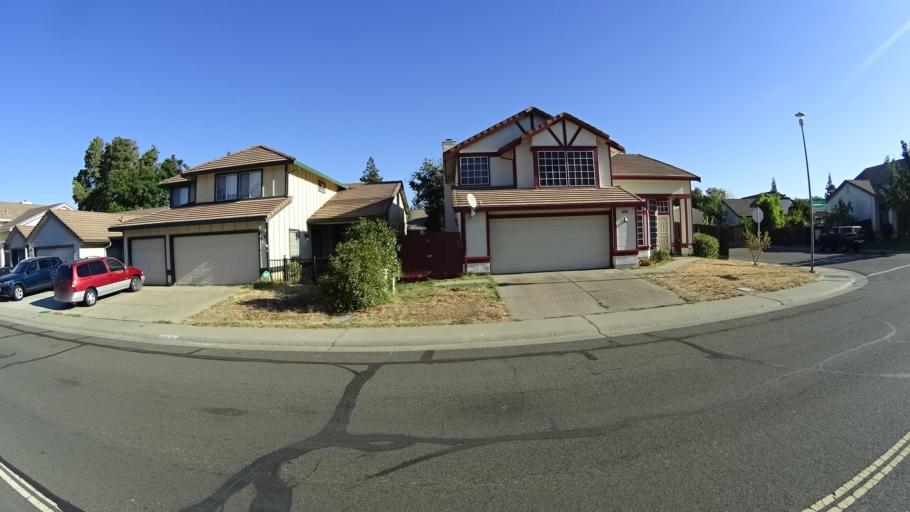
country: US
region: California
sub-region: Sacramento County
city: Elk Grove
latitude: 38.4349
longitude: -121.3772
